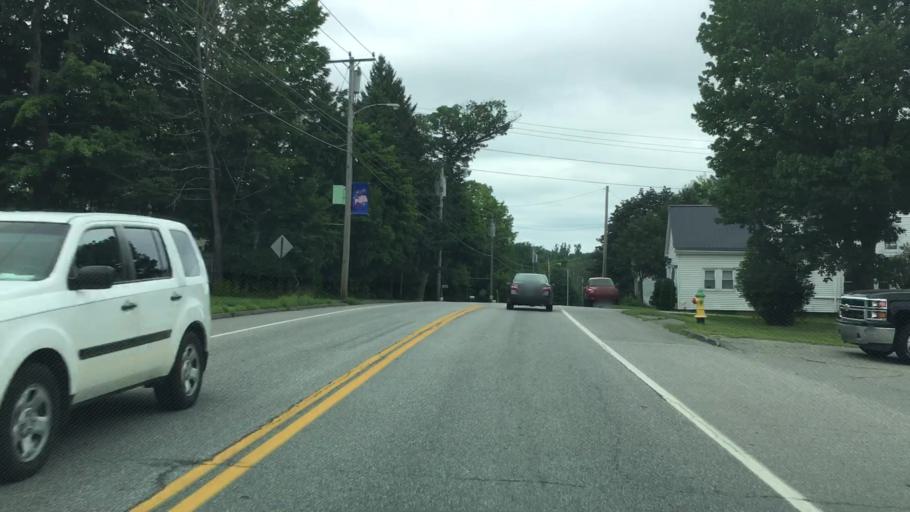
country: US
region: Maine
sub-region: Penobscot County
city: Hampden
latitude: 44.7331
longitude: -68.8416
